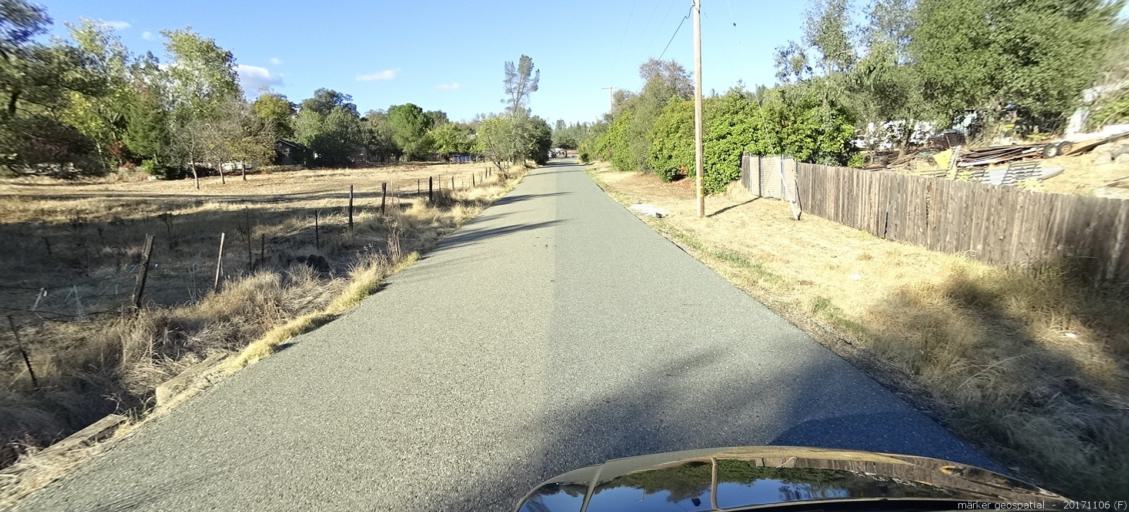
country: US
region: California
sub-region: Shasta County
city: Shasta
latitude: 40.5937
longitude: -122.4885
